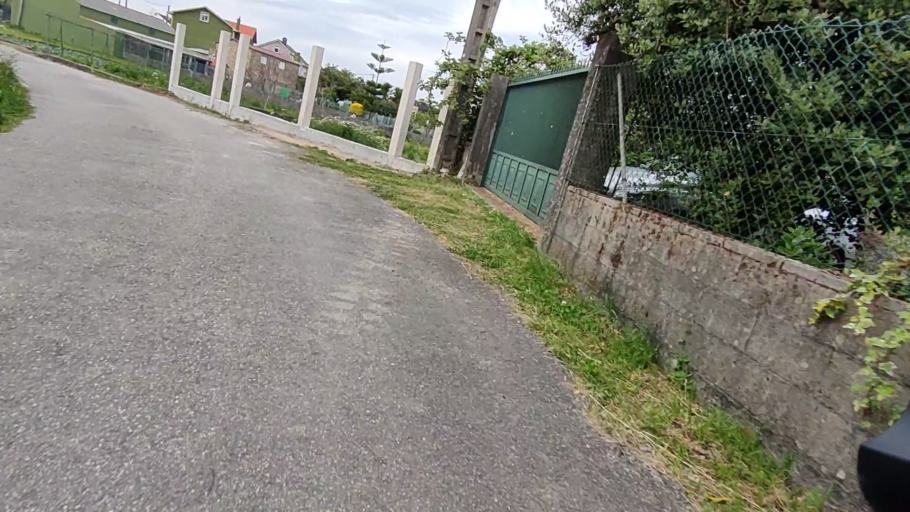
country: ES
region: Galicia
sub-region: Provincia da Coruna
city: Boiro
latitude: 42.6326
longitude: -8.8634
